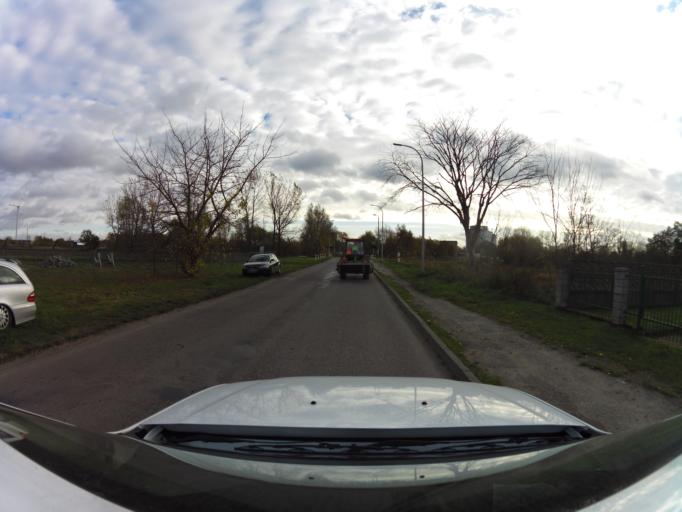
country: PL
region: West Pomeranian Voivodeship
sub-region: Powiat gryficki
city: Gryfice
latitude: 53.9261
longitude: 15.1953
